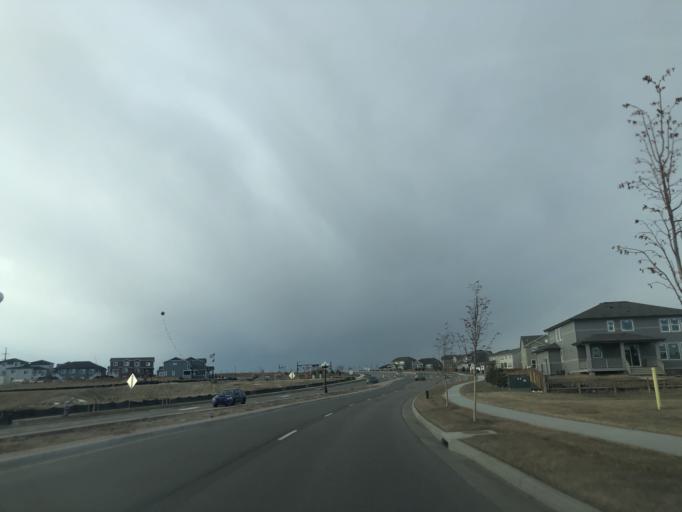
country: US
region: Colorado
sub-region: Douglas County
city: Stonegate
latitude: 39.5545
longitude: -104.8025
